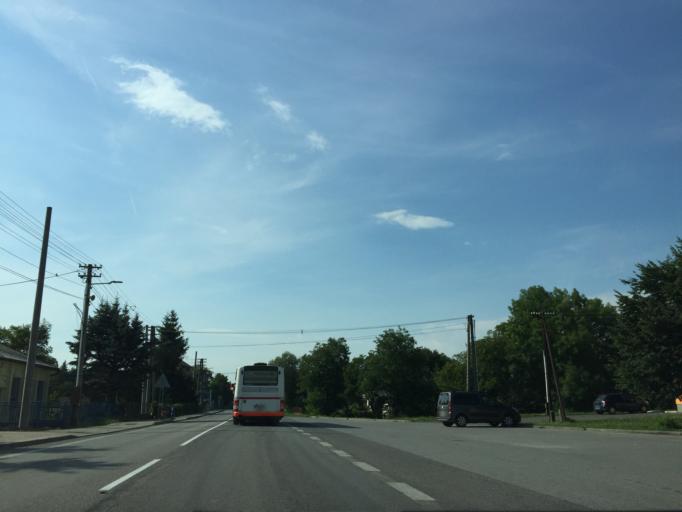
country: SK
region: Presovsky
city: Vranov nad Topl'ou
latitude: 48.9276
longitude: 21.5974
